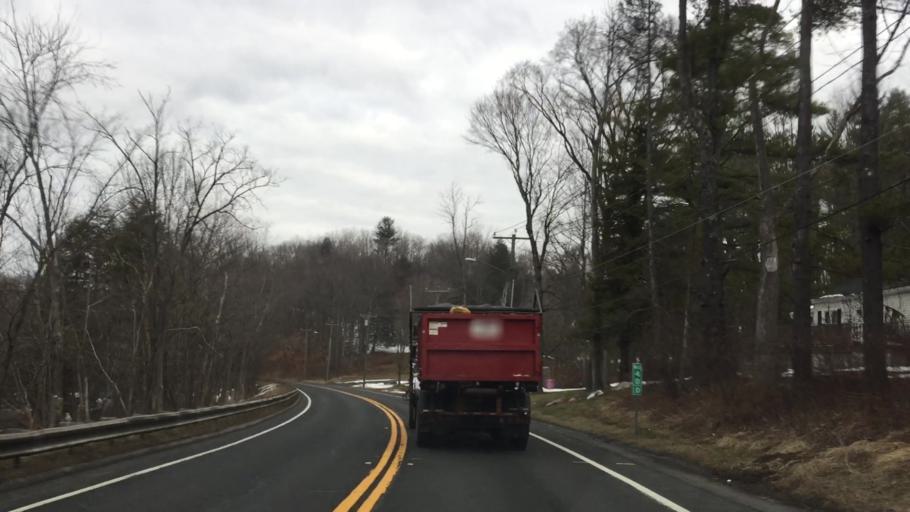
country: US
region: Massachusetts
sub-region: Berkshire County
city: Hinsdale
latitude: 42.4615
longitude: -73.1330
